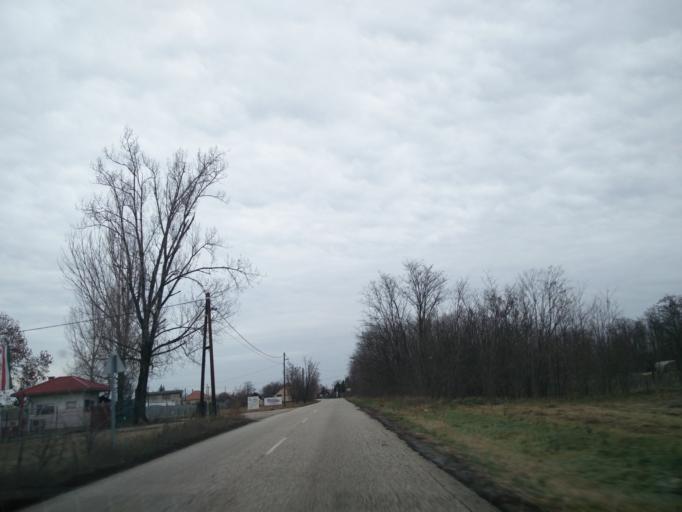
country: HU
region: Pest
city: Koka
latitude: 47.4720
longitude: 19.5619
